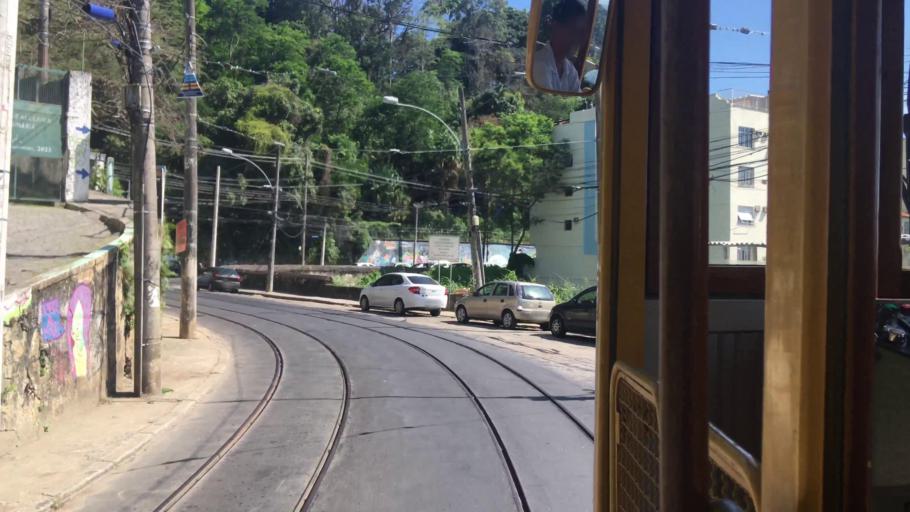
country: BR
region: Rio de Janeiro
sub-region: Rio De Janeiro
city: Rio de Janeiro
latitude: -22.9284
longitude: -43.1940
